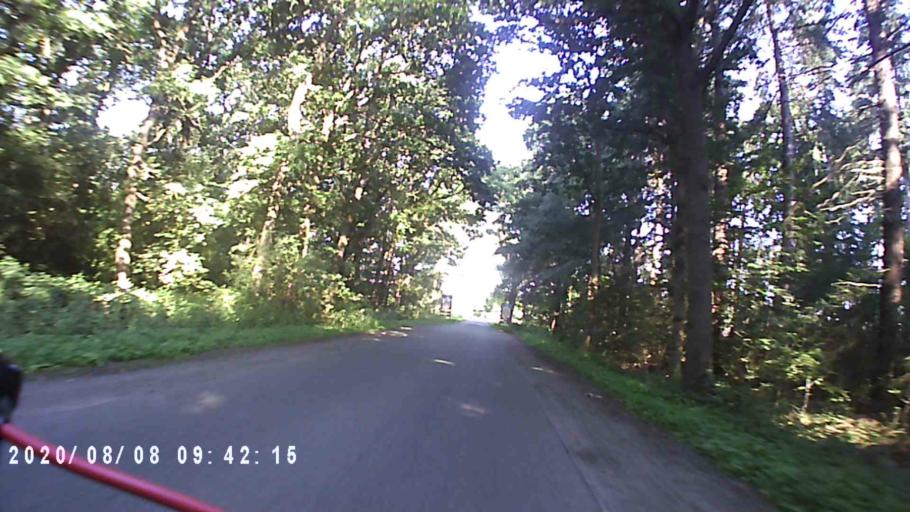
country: NL
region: Groningen
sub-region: Gemeente Leek
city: Leek
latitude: 53.0671
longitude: 6.3988
